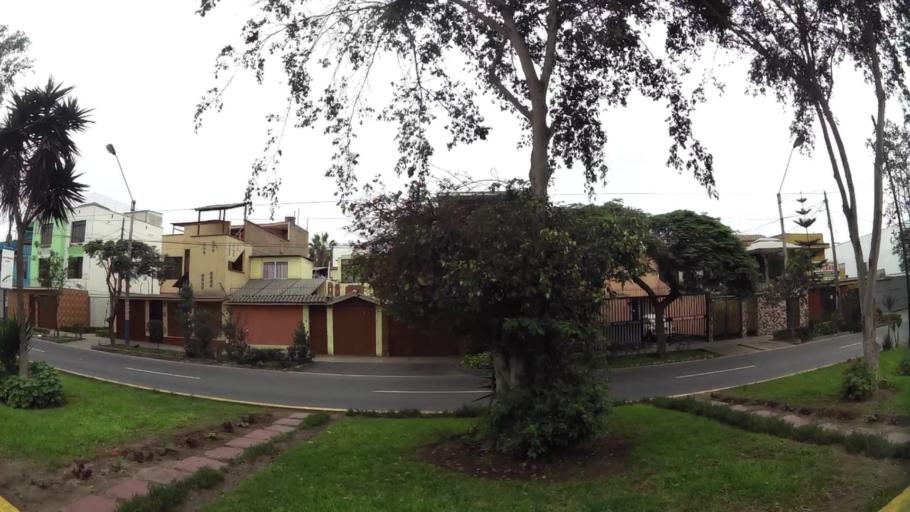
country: PE
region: Lima
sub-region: Lima
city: San Luis
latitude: -12.0751
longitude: -76.9930
